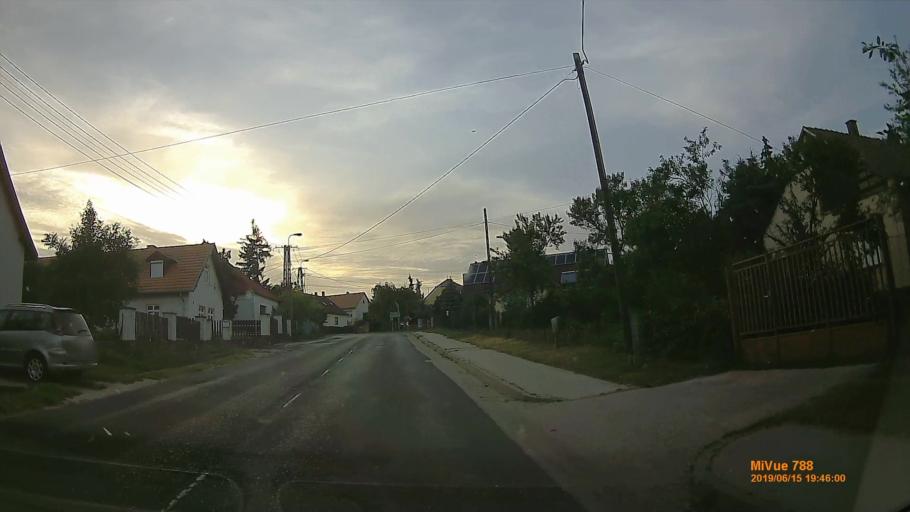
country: HU
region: Veszprem
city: Szentkiralyszabadja
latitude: 47.0128
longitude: 17.9597
